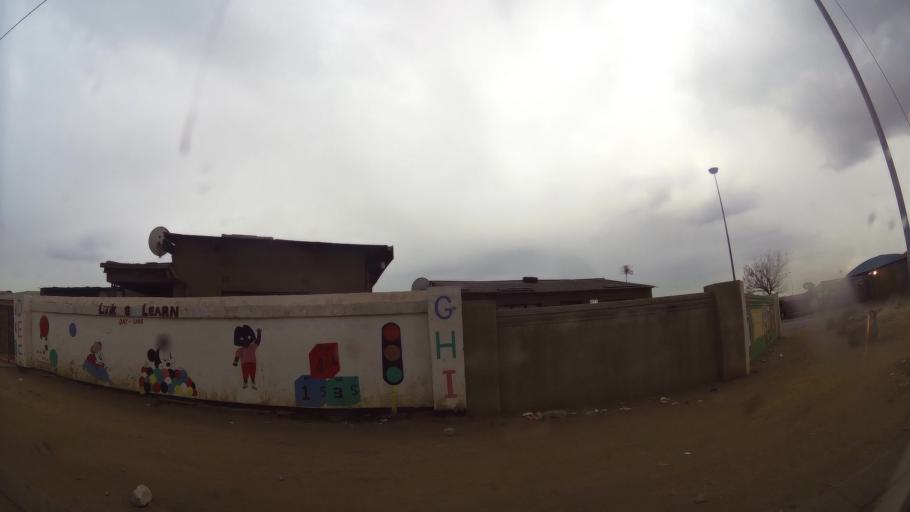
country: ZA
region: Gauteng
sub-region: Ekurhuleni Metropolitan Municipality
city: Germiston
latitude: -26.3442
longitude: 28.1440
